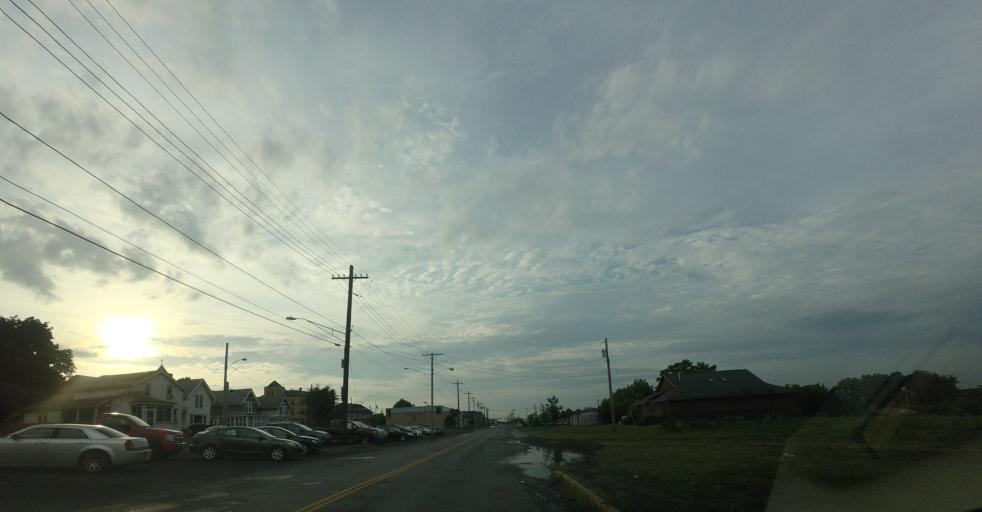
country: US
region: New York
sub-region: Onondaga County
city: Solvay
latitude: 43.0500
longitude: -76.1813
